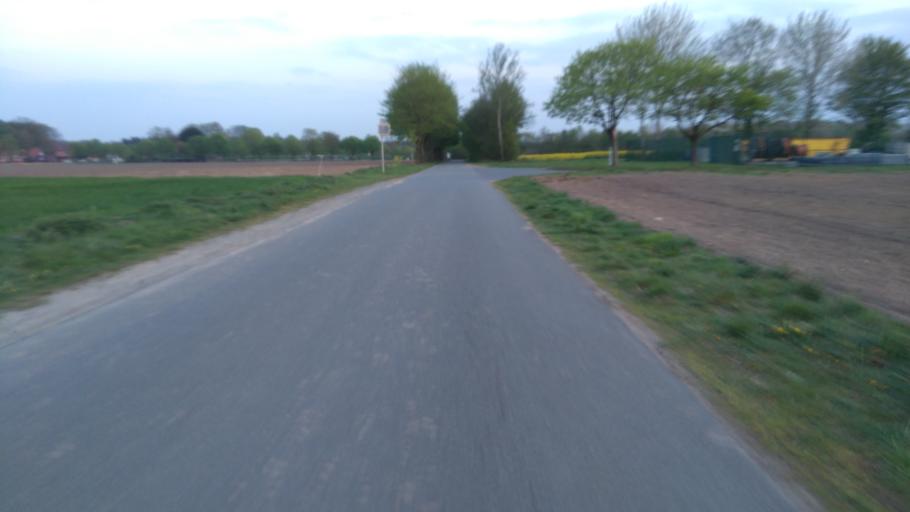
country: DE
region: Lower Saxony
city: Bargstedt
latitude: 53.4680
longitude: 9.4672
